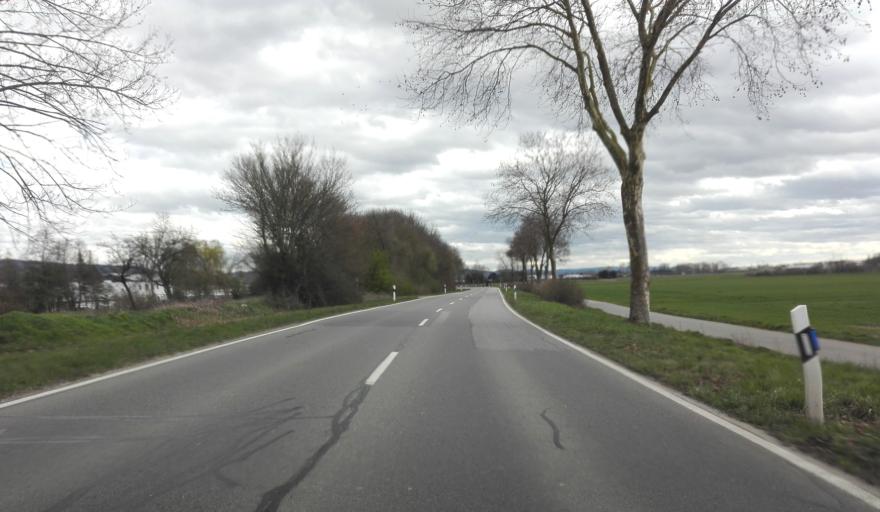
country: DE
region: Hesse
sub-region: Regierungsbezirk Darmstadt
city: Einhausen
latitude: 49.6902
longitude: 8.5823
